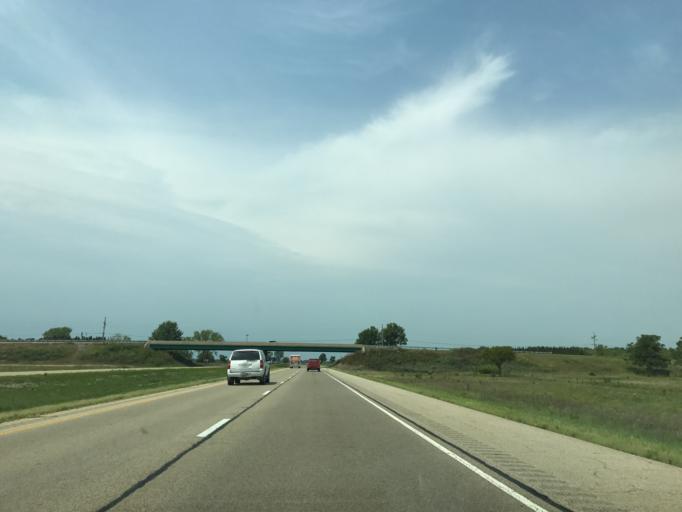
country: US
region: Illinois
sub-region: Bureau County
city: Ladd
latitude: 41.3673
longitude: -89.2162
